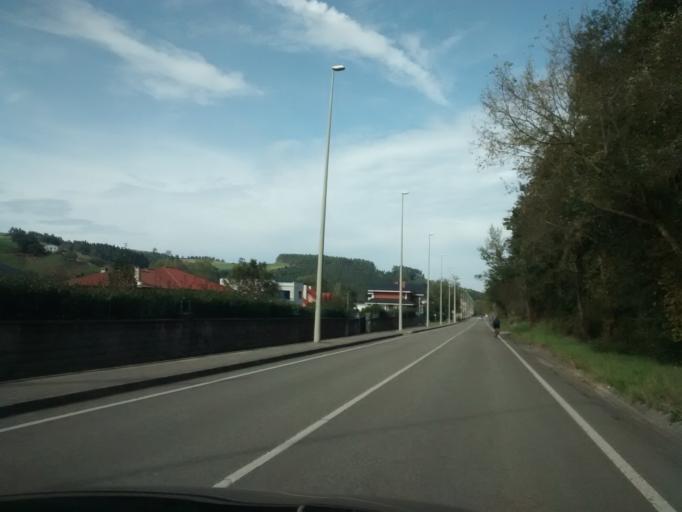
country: ES
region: Cantabria
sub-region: Provincia de Cantabria
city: Entrambasaguas
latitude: 43.3557
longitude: -3.7090
